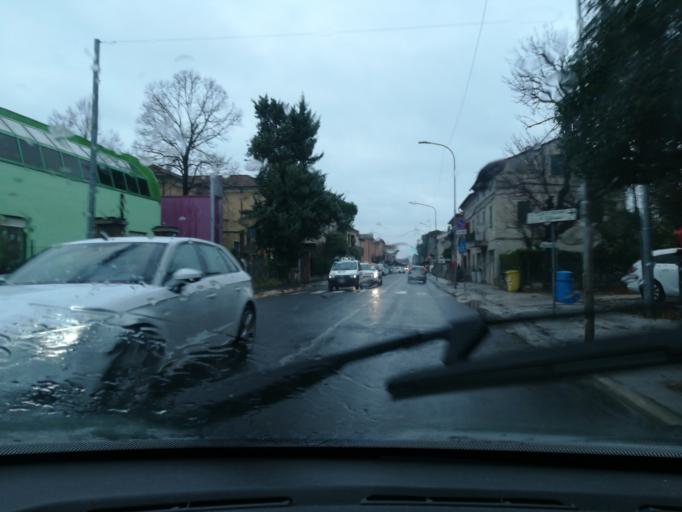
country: IT
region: The Marches
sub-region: Provincia di Macerata
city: Sforzacosta
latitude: 43.2582
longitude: 13.4206
